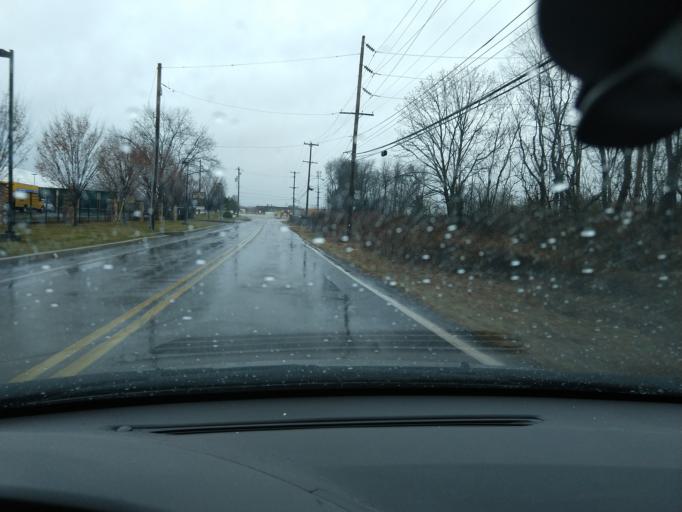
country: US
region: Pennsylvania
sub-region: Chester County
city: Kenilworth
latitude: 40.2353
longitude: -75.6222
